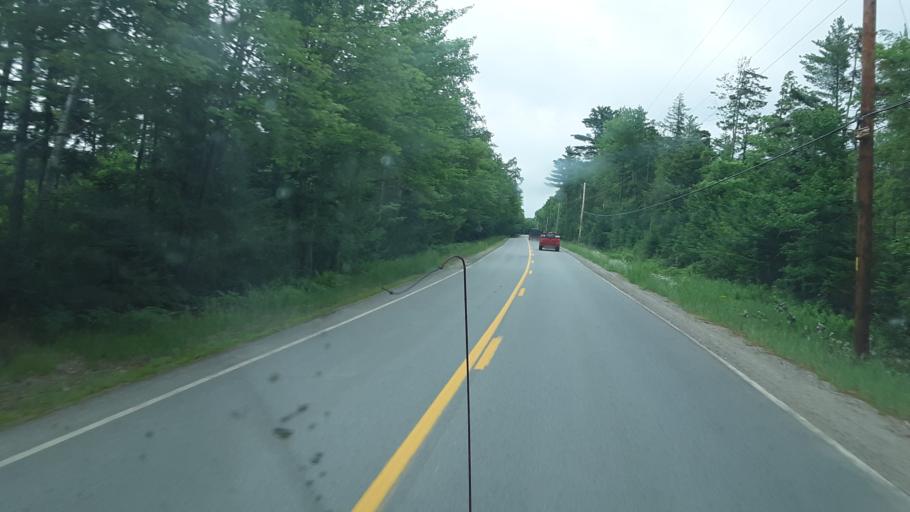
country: US
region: Maine
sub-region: Penobscot County
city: Millinocket
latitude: 45.6790
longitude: -68.7558
